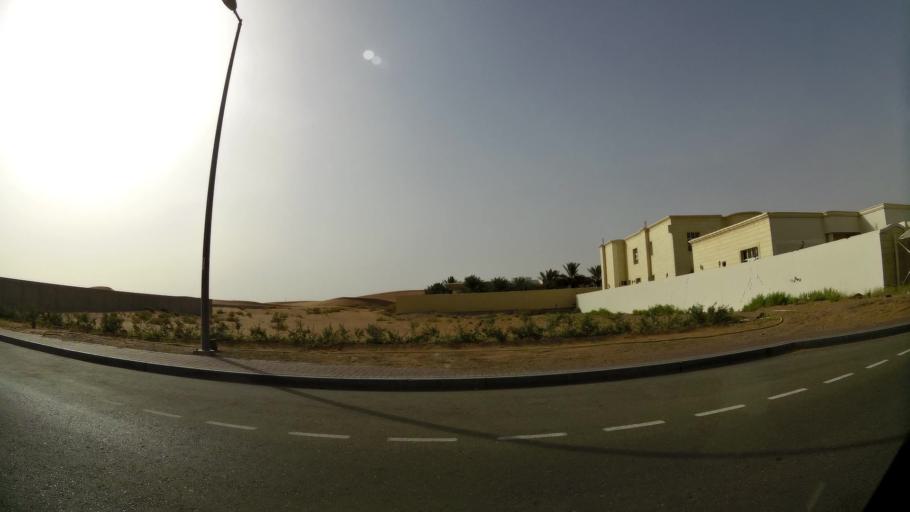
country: AE
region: Abu Dhabi
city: Al Ain
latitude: 24.2026
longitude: 55.6108
